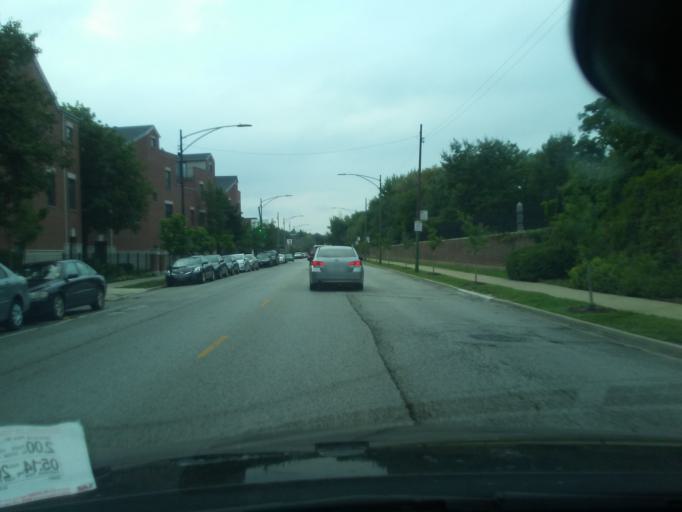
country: US
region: Illinois
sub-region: Cook County
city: Lincolnwood
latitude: 41.9552
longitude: -87.6628
